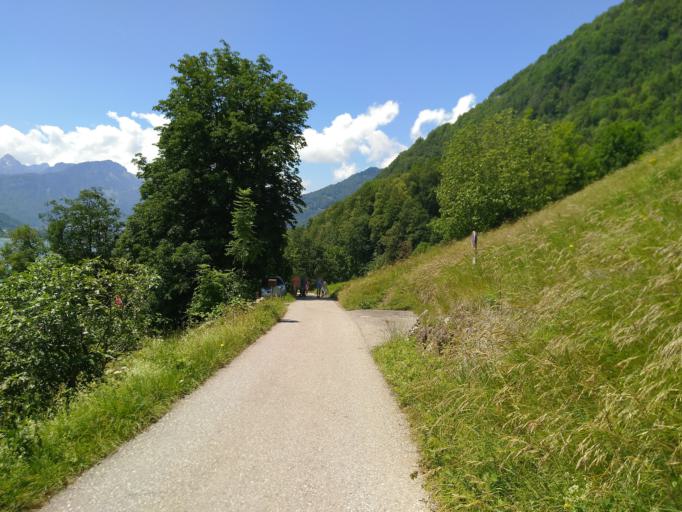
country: CH
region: Saint Gallen
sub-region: Wahlkreis See-Gaster
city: Amden
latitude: 47.1363
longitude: 9.1552
